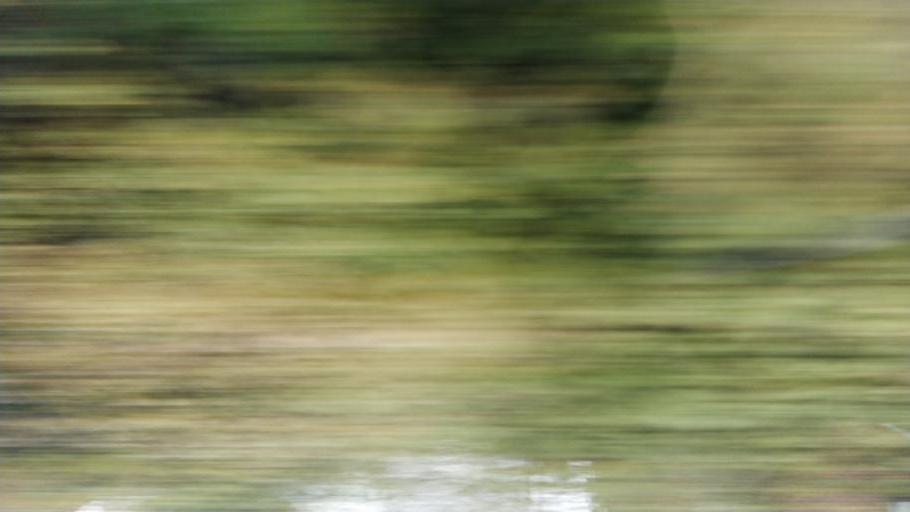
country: GB
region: England
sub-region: Borough of Wigan
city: Atherton
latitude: 53.5299
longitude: -2.4818
